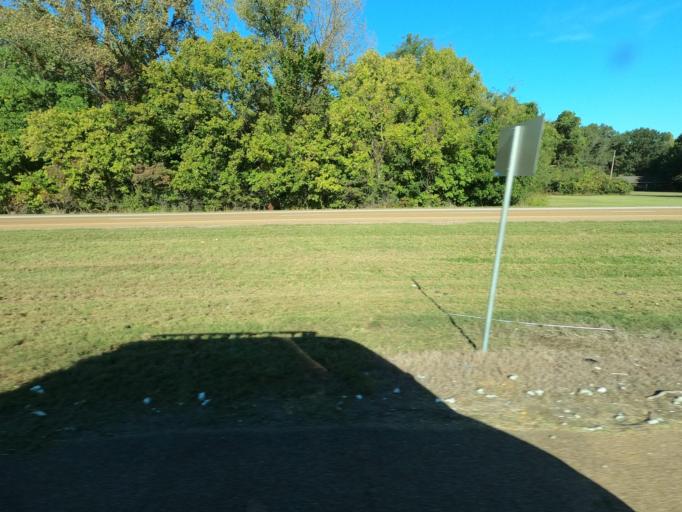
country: US
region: Tennessee
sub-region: Shelby County
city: Millington
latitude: 35.3670
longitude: -89.8864
